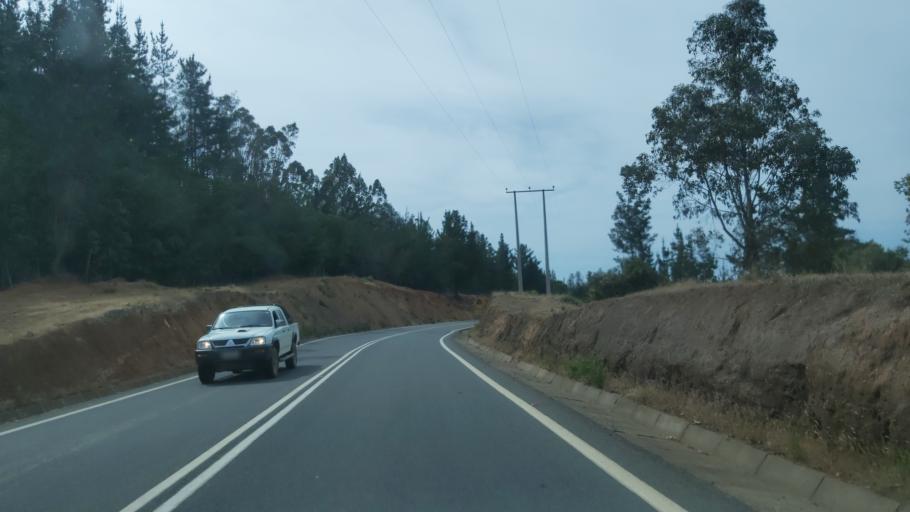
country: CL
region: Maule
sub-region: Provincia de Talca
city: Constitucion
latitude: -34.9151
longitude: -71.9947
